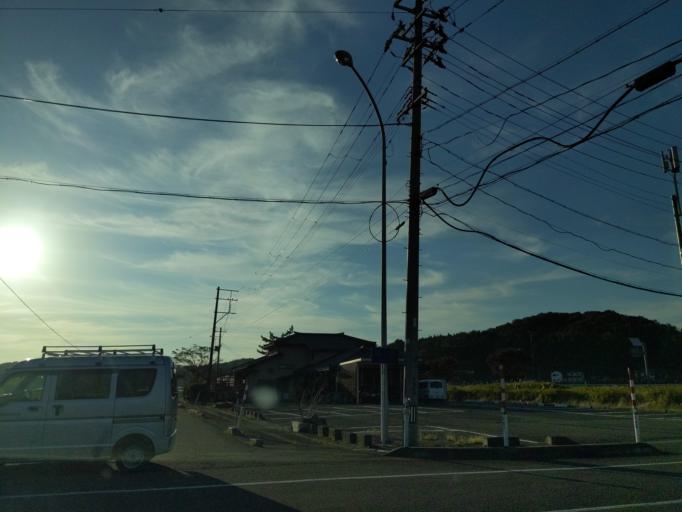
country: JP
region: Niigata
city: Nagaoka
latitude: 37.5771
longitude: 138.7533
